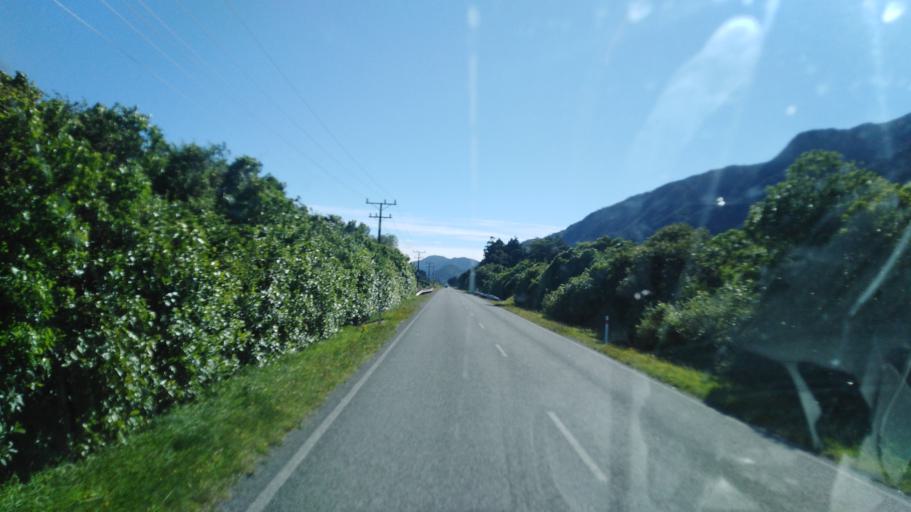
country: NZ
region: West Coast
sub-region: Buller District
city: Westport
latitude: -41.6592
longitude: 171.8193
